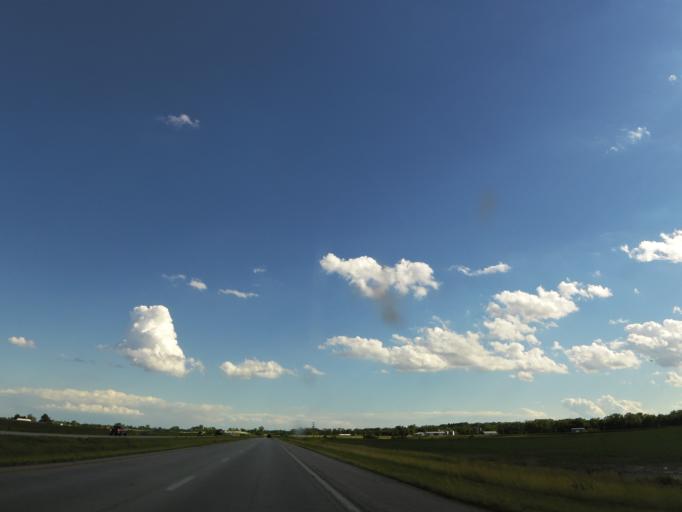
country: US
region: Illinois
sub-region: Adams County
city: Quincy
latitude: 39.9490
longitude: -91.5189
